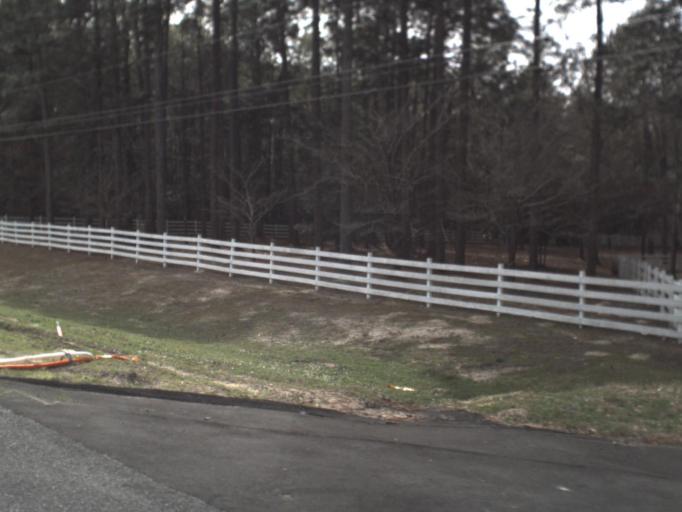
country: US
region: Florida
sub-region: Bay County
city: Youngstown
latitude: 30.4467
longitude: -85.4258
